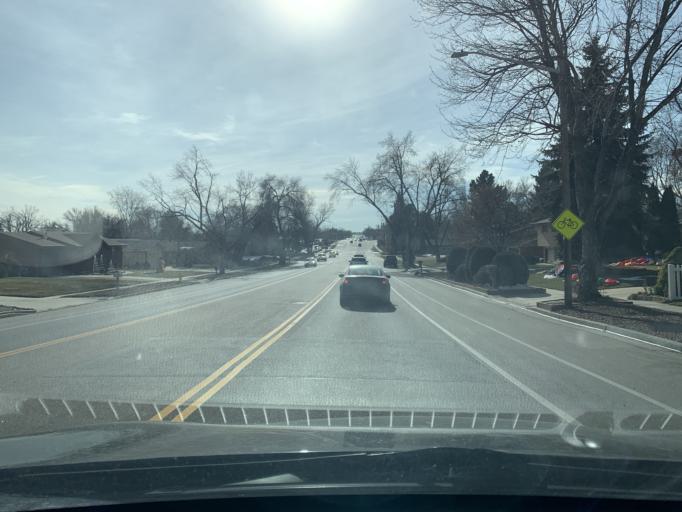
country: US
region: Colorado
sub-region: Jefferson County
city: Arvada
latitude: 39.8162
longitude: -105.1380
